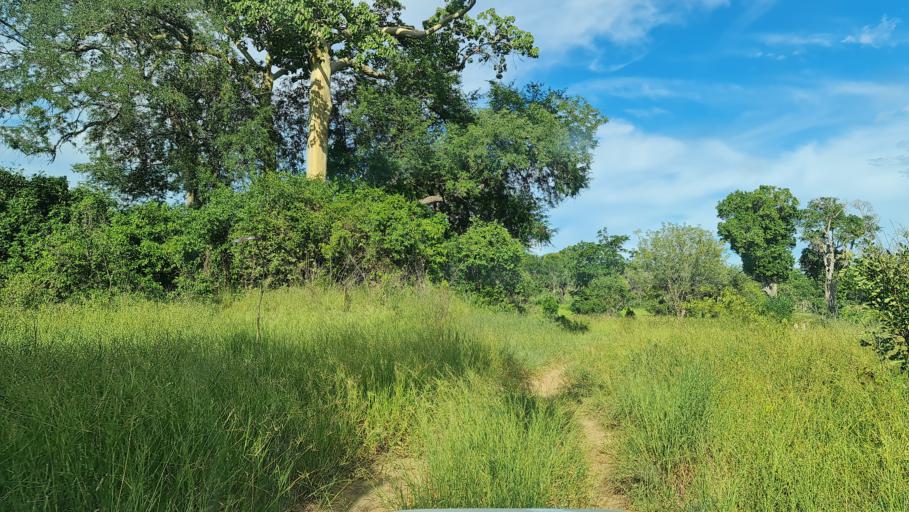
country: MZ
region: Nampula
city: Ilha de Mocambique
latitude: -15.5042
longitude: 40.1554
